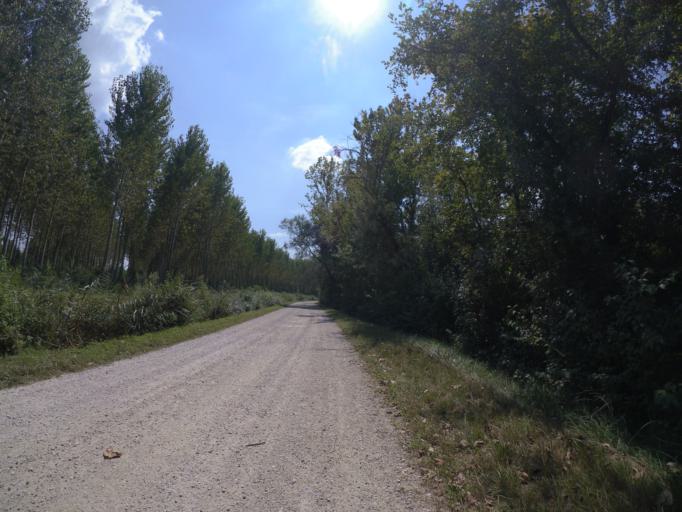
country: IT
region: Friuli Venezia Giulia
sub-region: Provincia di Udine
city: Bertiolo
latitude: 45.9170
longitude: 13.0620
